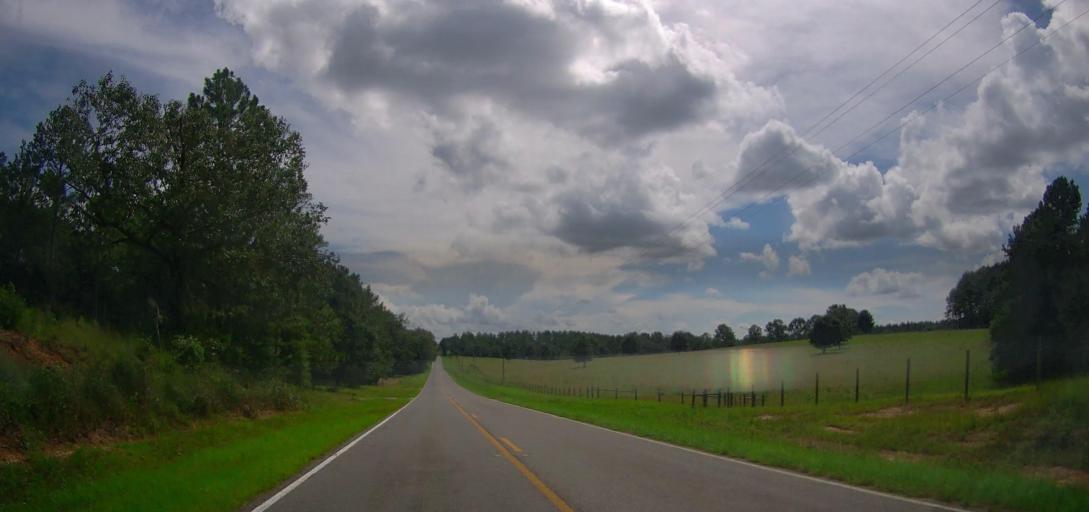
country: US
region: Georgia
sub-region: Taylor County
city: Butler
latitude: 32.4547
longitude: -84.1957
